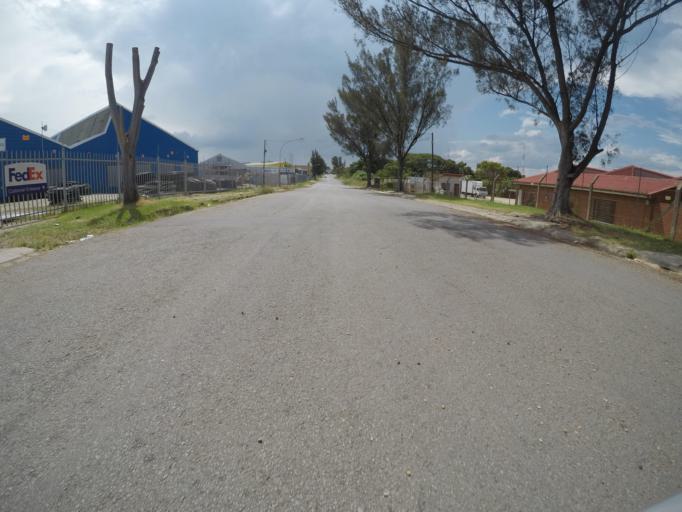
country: ZA
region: Eastern Cape
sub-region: Buffalo City Metropolitan Municipality
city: East London
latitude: -33.0364
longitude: 27.8757
